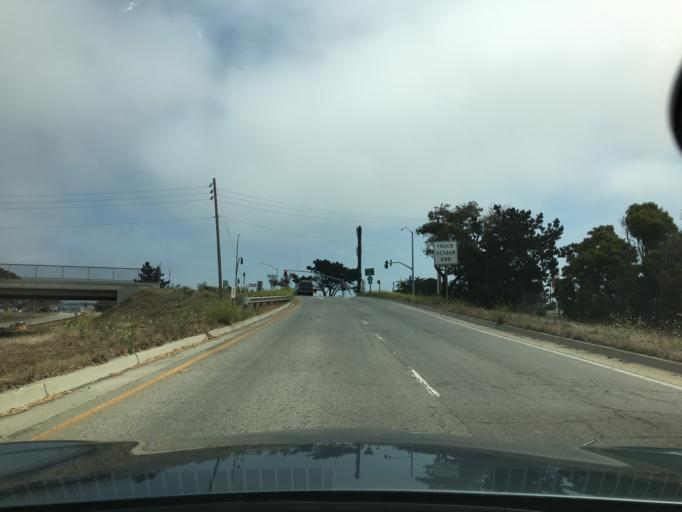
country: US
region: California
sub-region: Monterey County
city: Castroville
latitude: 36.7606
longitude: -121.7529
